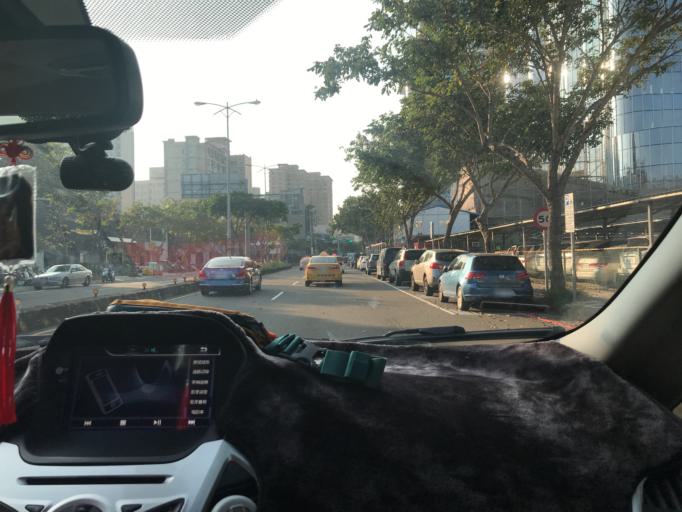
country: TW
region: Taiwan
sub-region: Hsinchu
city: Zhubei
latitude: 24.8063
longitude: 121.0390
